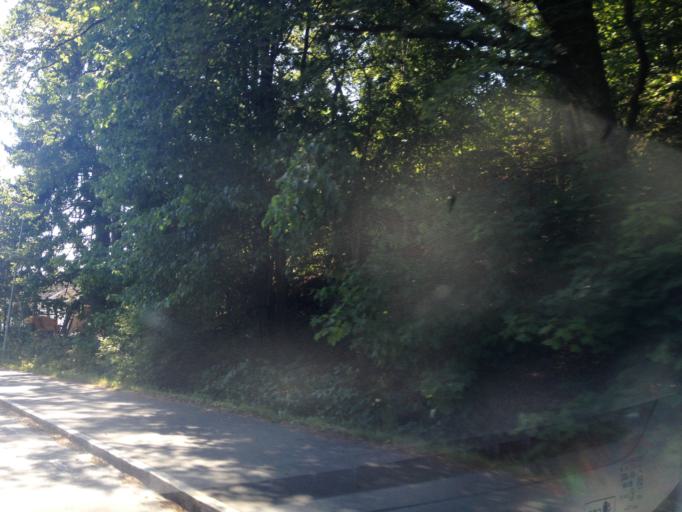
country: SE
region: Vaestra Goetaland
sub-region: Alingsas Kommun
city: Ingared
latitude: 57.8532
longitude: 12.4544
